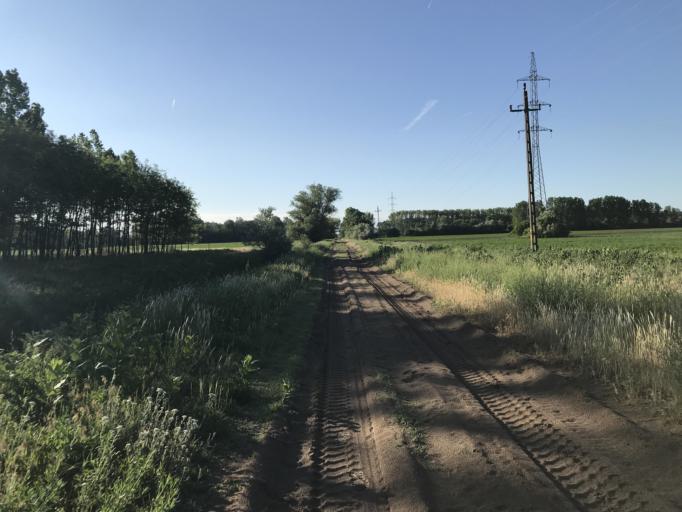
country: HU
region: Bacs-Kiskun
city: Tiszakecske
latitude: 46.9696
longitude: 20.0665
